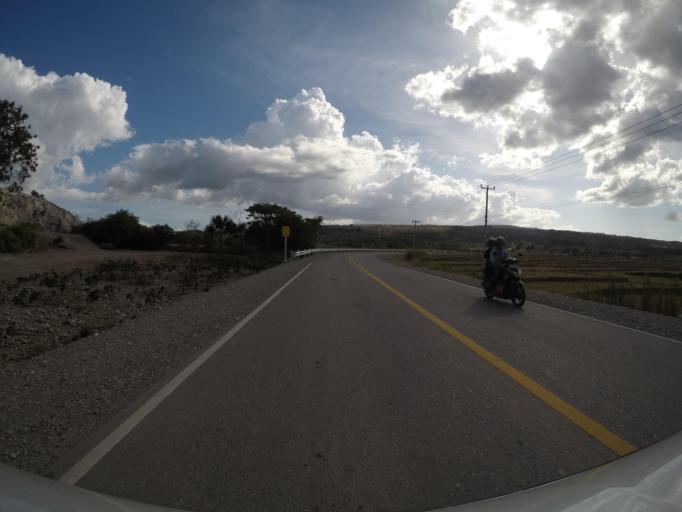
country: TL
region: Baucau
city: Baucau
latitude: -8.4733
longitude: 126.5029
